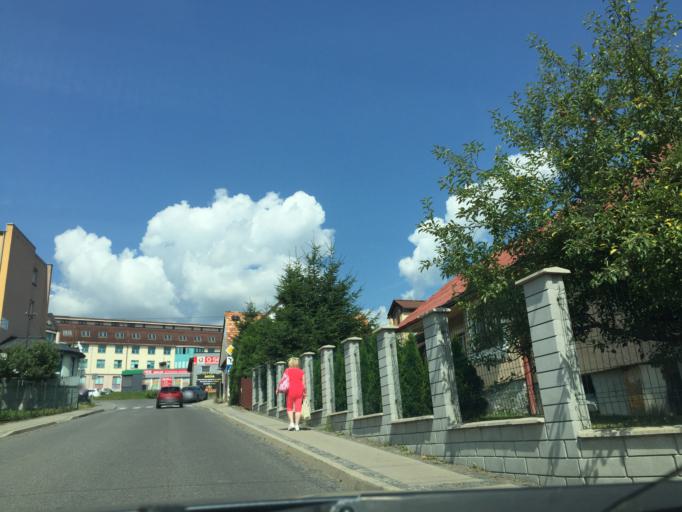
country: SK
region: Zilinsky
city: Namestovo
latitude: 49.4045
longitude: 19.4762
